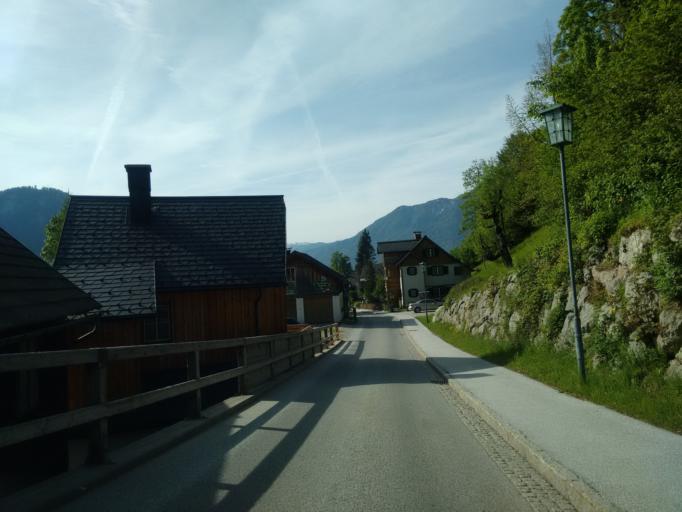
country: AT
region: Styria
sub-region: Politischer Bezirk Liezen
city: Altaussee
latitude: 47.6421
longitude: 13.7624
